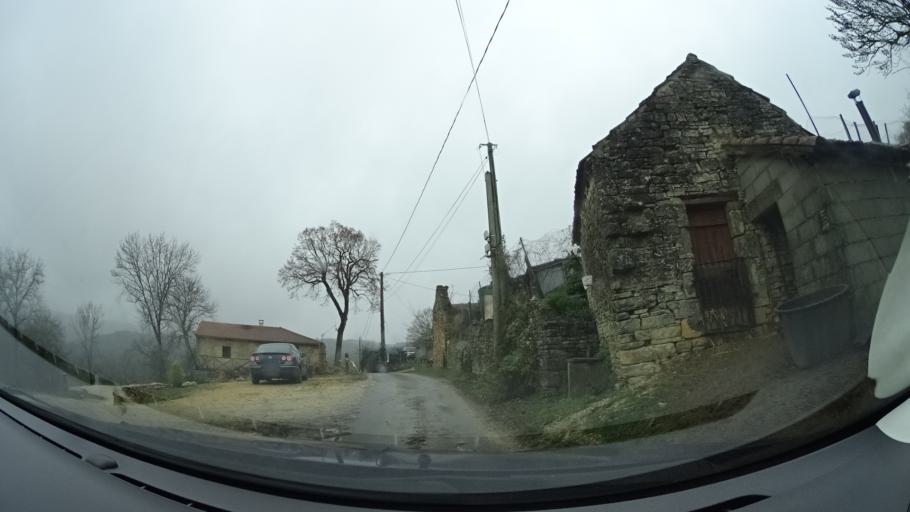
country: FR
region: Aquitaine
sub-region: Departement de la Dordogne
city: Cenac-et-Saint-Julien
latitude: 44.7387
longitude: 1.1547
